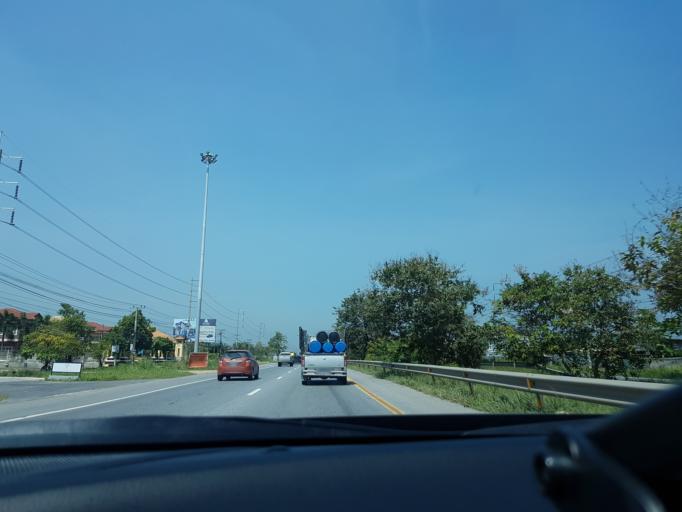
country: TH
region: Sara Buri
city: Saraburi
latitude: 14.5068
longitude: 100.9091
